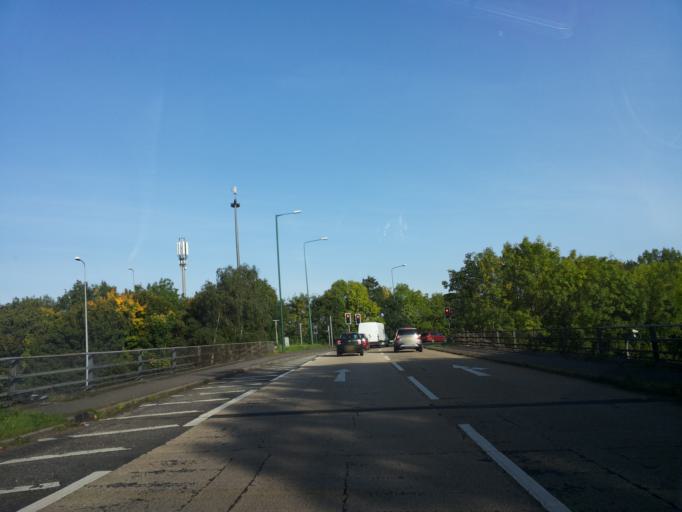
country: GB
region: England
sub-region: Solihull
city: Knowle
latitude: 52.4045
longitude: -1.7503
